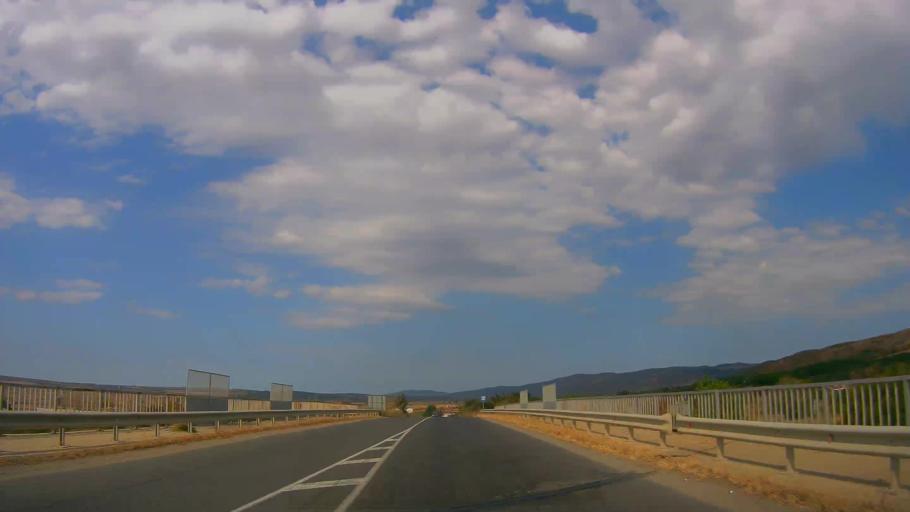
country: BG
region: Burgas
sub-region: Obshtina Aytos
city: Aytos
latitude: 42.7040
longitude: 27.2419
